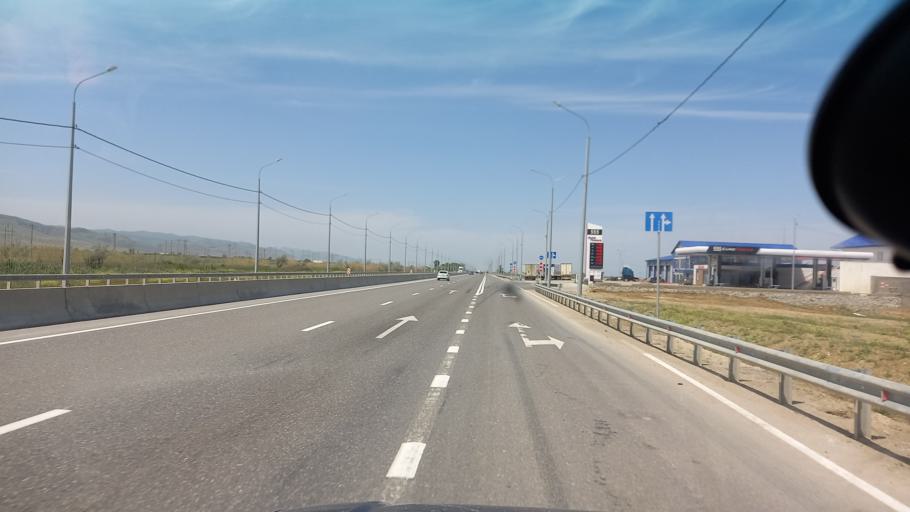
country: RU
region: Dagestan
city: Manas
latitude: 42.7413
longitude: 47.6594
